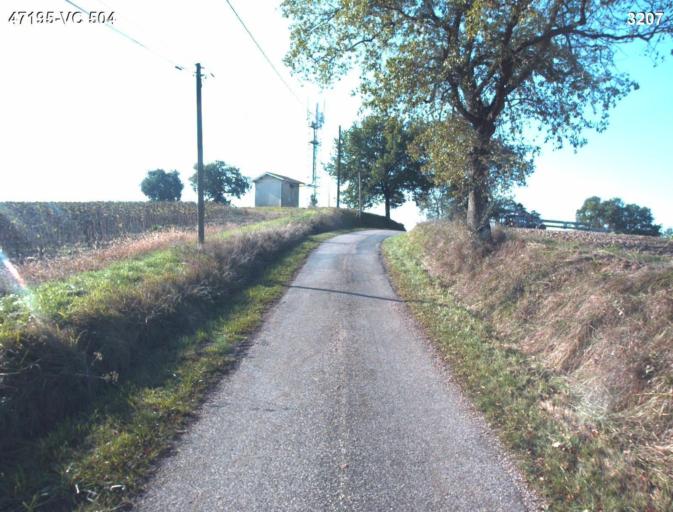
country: FR
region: Aquitaine
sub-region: Departement du Lot-et-Garonne
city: Vianne
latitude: 44.1730
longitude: 0.3434
